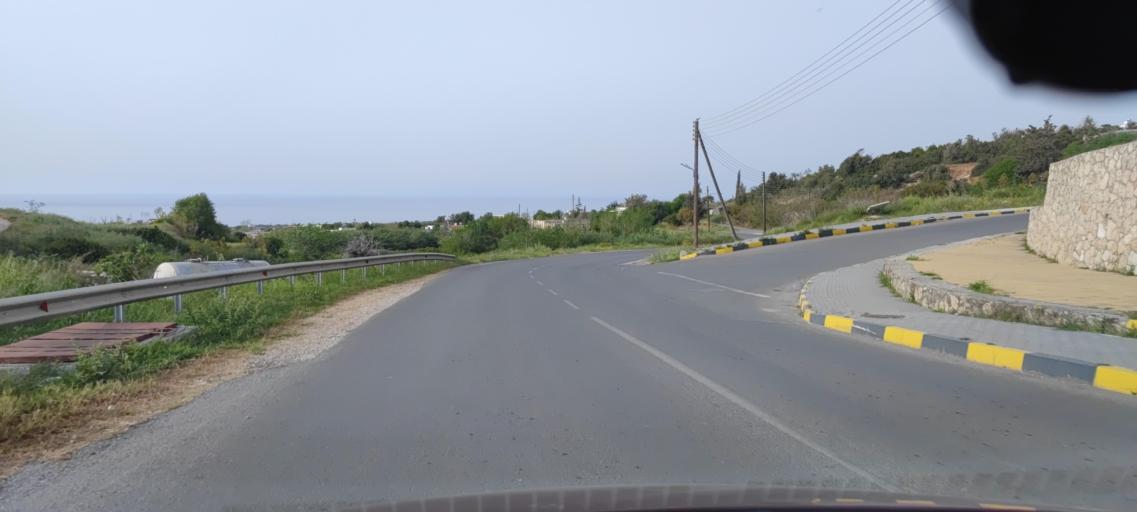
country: CY
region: Ammochostos
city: Leonarisso
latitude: 35.5360
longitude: 34.1925
